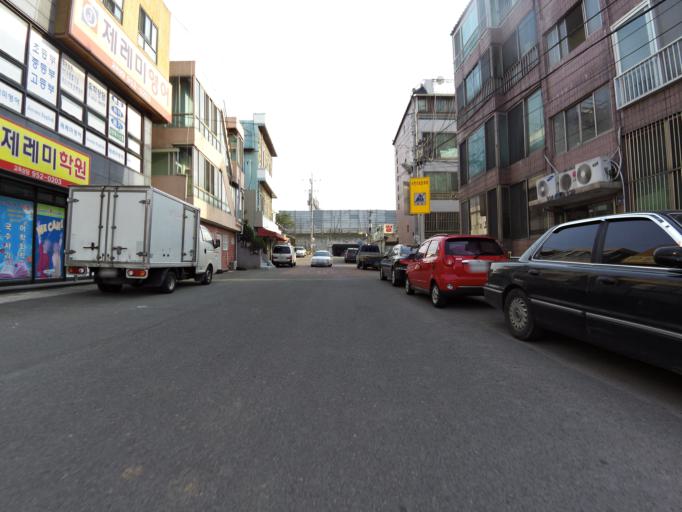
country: KR
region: Daegu
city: Daegu
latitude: 35.8748
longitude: 128.6498
